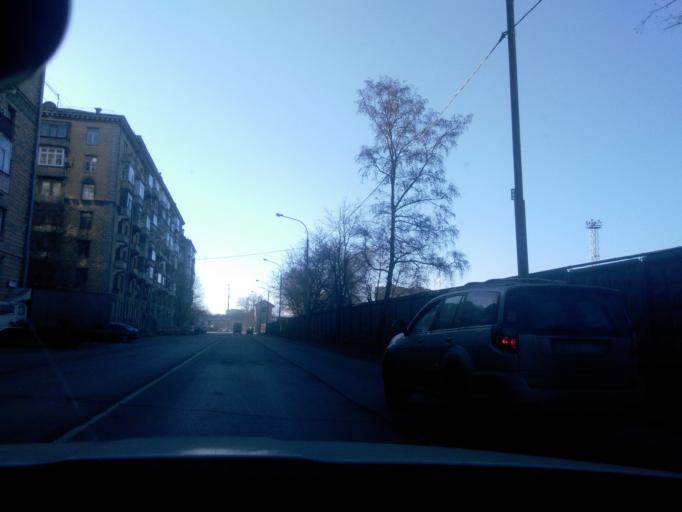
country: RU
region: Moscow
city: Sokol
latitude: 55.8005
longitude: 37.4986
